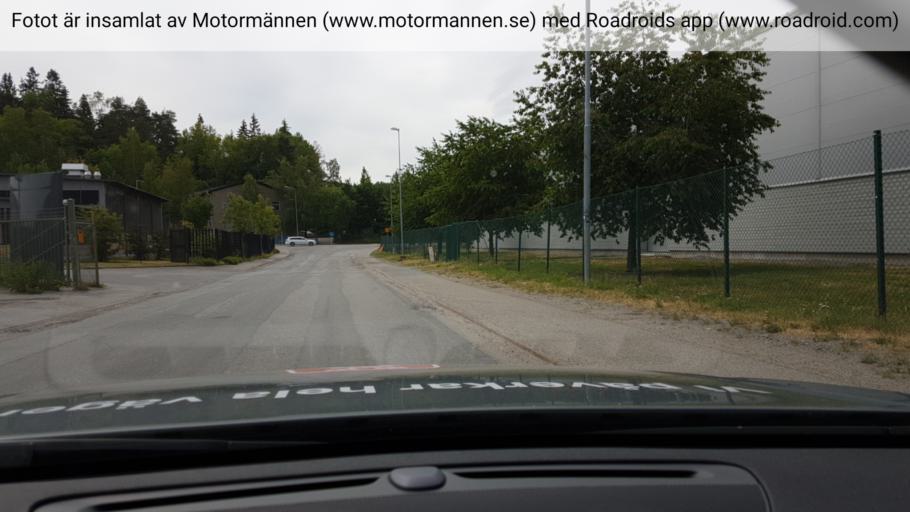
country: SE
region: Stockholm
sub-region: Huddinge Kommun
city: Huddinge
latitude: 59.2318
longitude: 17.9854
